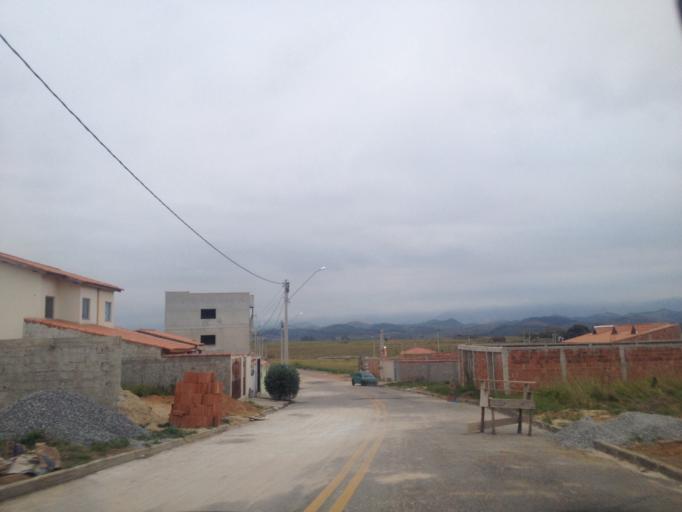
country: BR
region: Rio de Janeiro
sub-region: Porto Real
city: Porto Real
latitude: -22.4198
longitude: -44.3105
